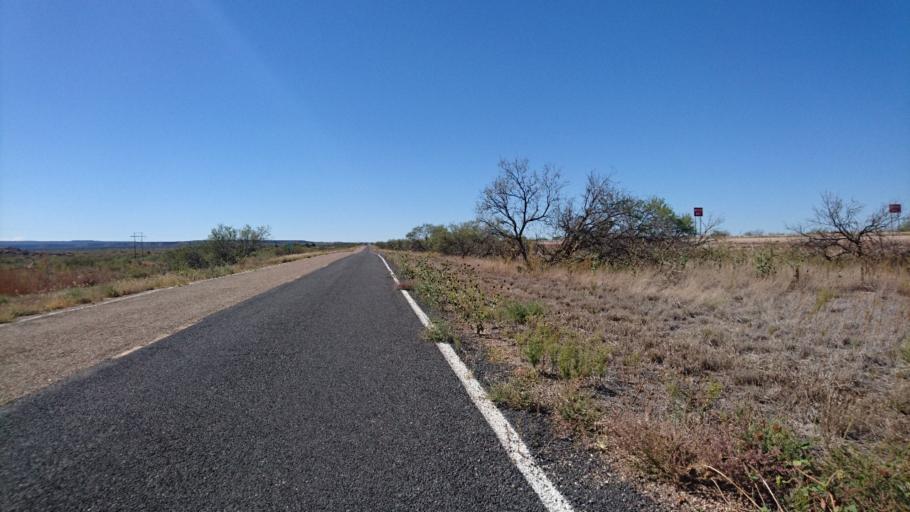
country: US
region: New Mexico
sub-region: Quay County
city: Tucumcari
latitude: 35.0789
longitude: -104.1273
